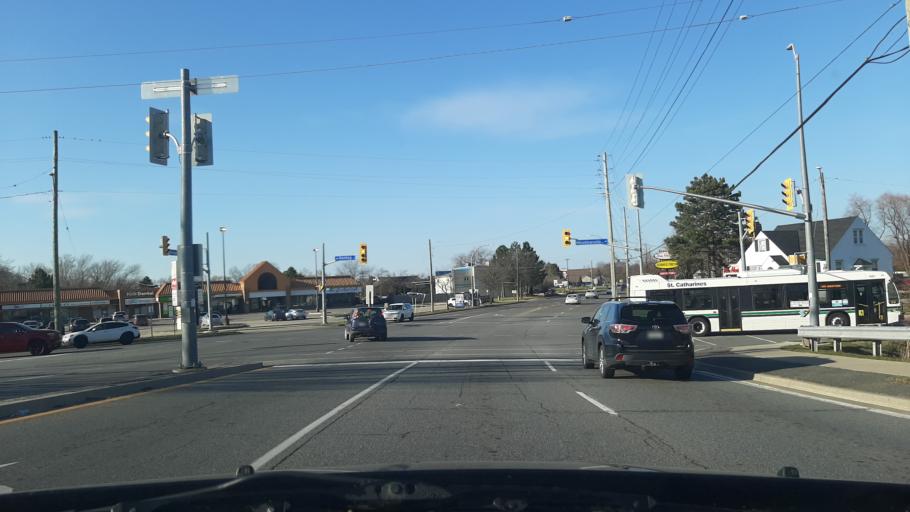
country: CA
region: Ontario
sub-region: Regional Municipality of Niagara
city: St. Catharines
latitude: 43.1809
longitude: -79.2672
